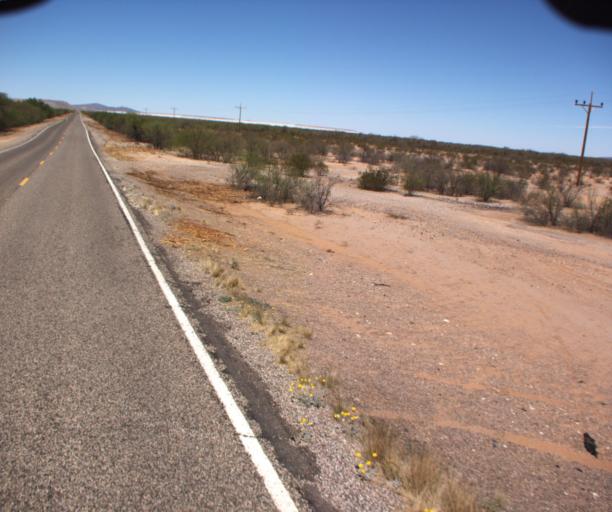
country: US
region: Arizona
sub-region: Pima County
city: Ajo
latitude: 32.3313
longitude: -112.7851
